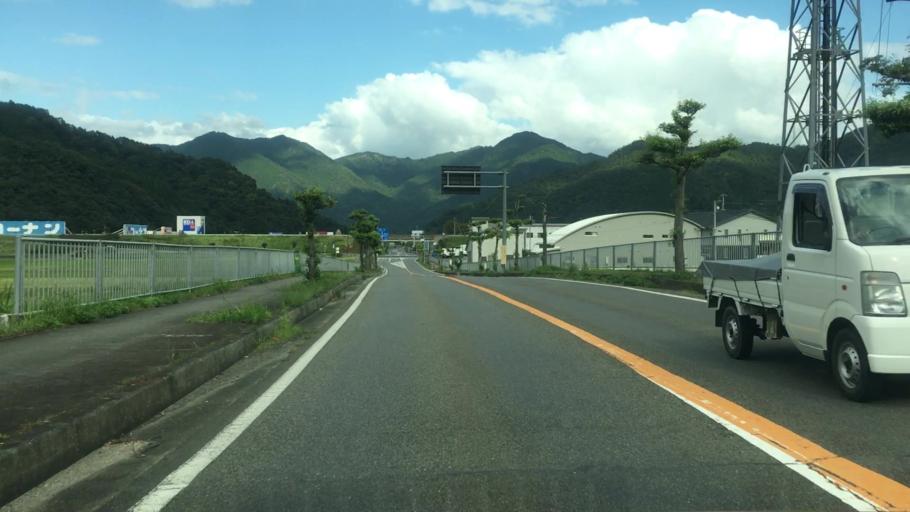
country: JP
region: Hyogo
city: Toyooka
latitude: 35.3797
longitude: 134.7783
